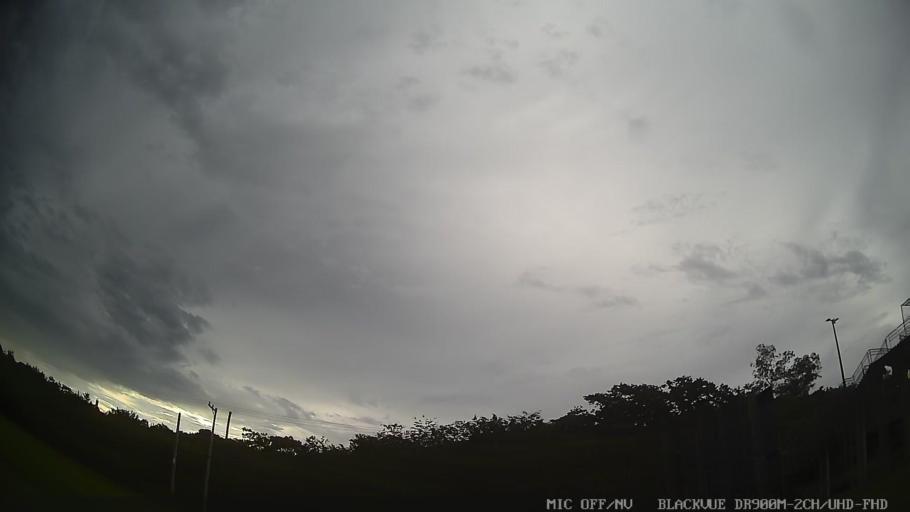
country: BR
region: Sao Paulo
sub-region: Jaguariuna
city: Jaguariuna
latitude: -22.7152
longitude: -47.0140
